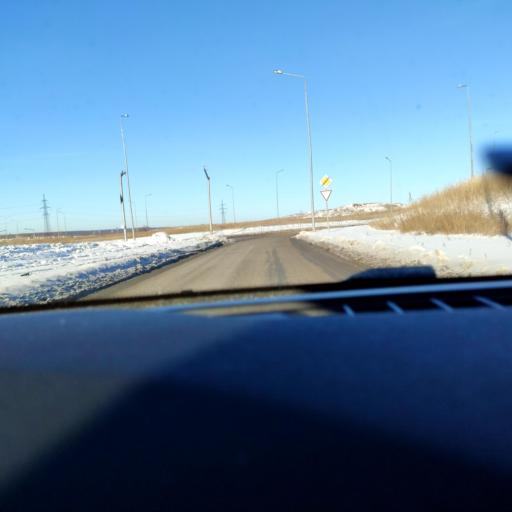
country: RU
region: Samara
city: Petra-Dubrava
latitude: 53.3104
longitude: 50.3437
